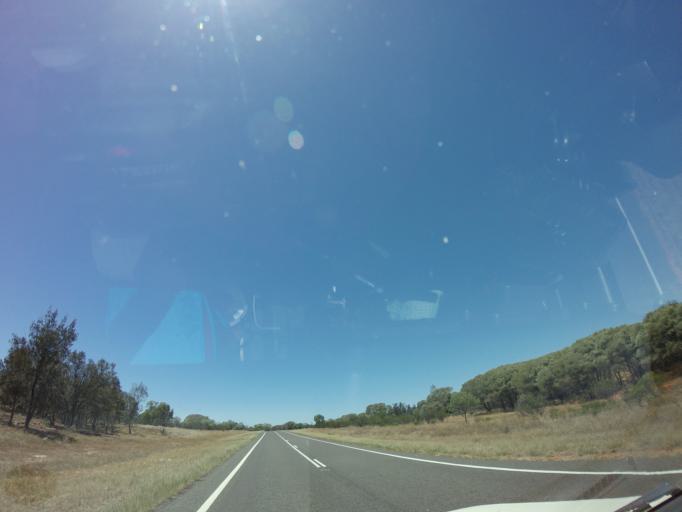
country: AU
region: New South Wales
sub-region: Cobar
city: Cobar
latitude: -31.5742
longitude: 144.7982
